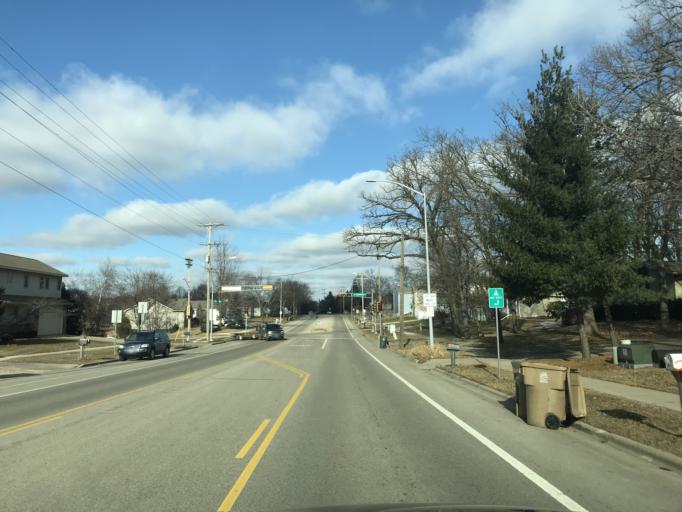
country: US
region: Wisconsin
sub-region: Dane County
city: Monona
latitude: 43.1132
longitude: -89.2961
